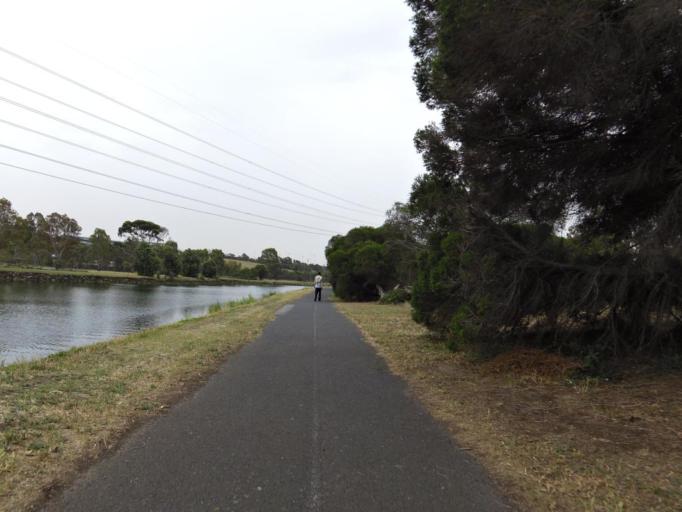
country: AU
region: Victoria
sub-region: Melbourne
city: Ascot Vale
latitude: -37.7817
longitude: 144.9005
